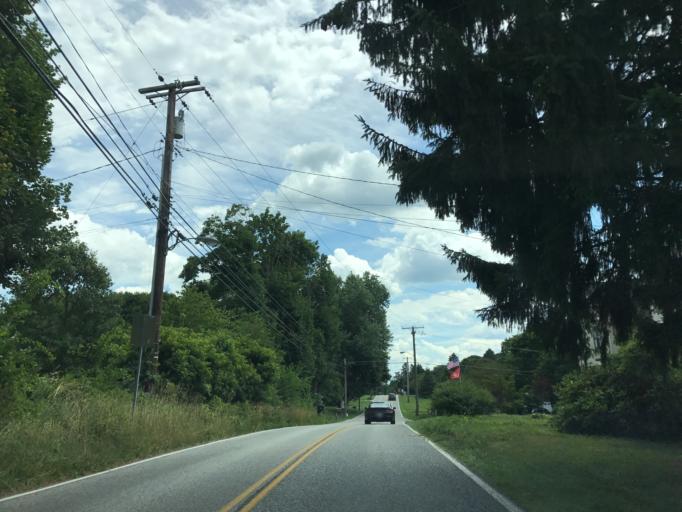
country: US
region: Maryland
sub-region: Harford County
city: Jarrettsville
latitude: 39.6011
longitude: -76.4886
